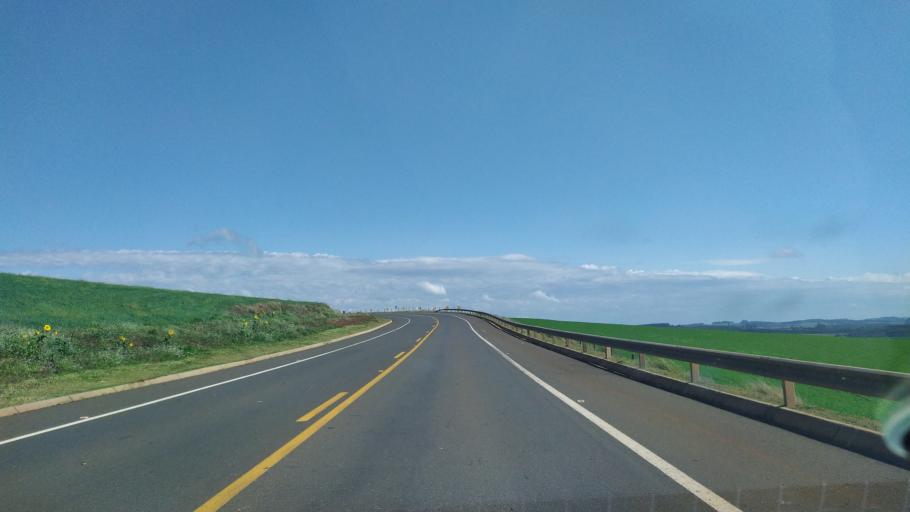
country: BR
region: Parana
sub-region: Ortigueira
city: Ortigueira
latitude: -24.2576
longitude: -50.8082
